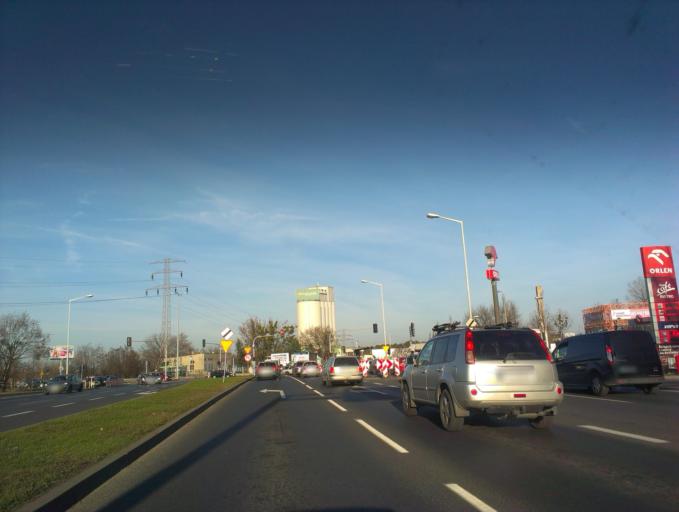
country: PL
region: Greater Poland Voivodeship
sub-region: Poznan
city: Poznan
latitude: 52.4265
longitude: 16.9660
